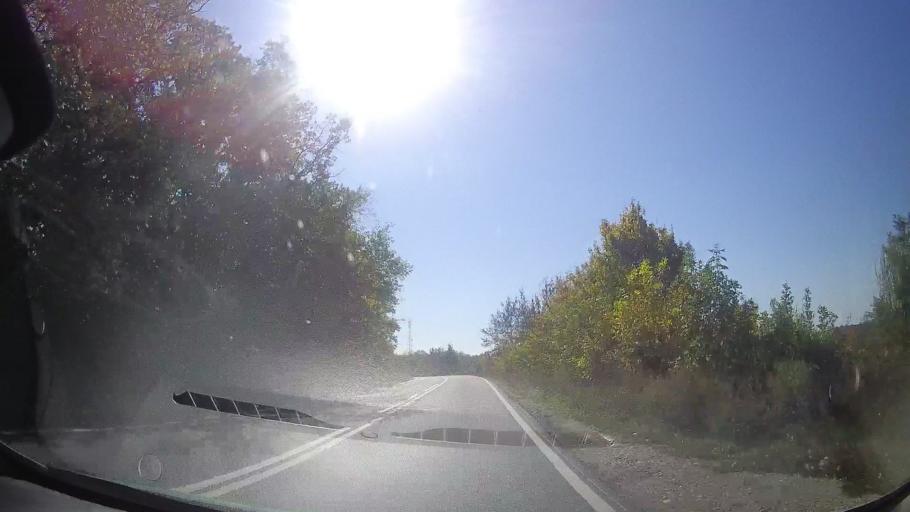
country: RO
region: Timis
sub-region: Municipiul Lugoj
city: Lugoj
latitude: 45.7090
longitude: 21.9660
